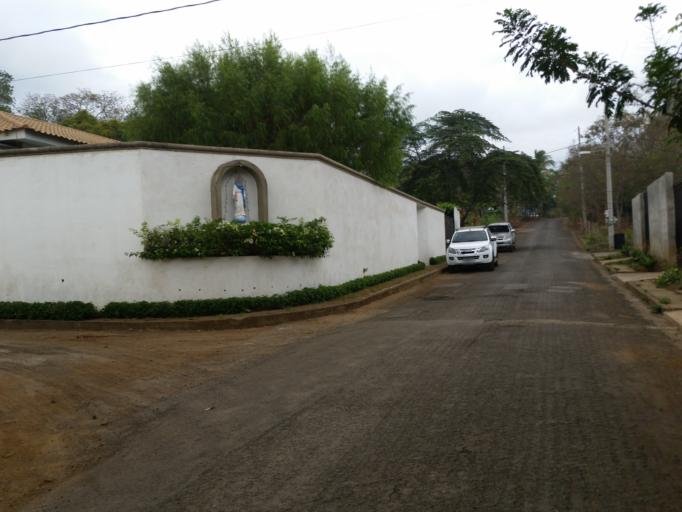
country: NI
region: Managua
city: Managua
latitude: 12.0747
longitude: -86.2533
